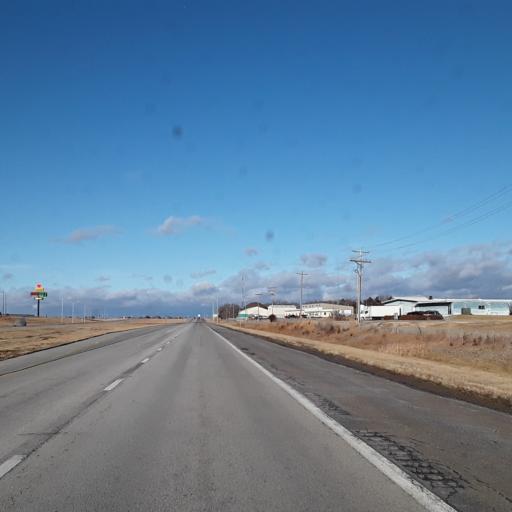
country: US
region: Kansas
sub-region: Republic County
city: Belleville
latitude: 39.8313
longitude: -97.6367
